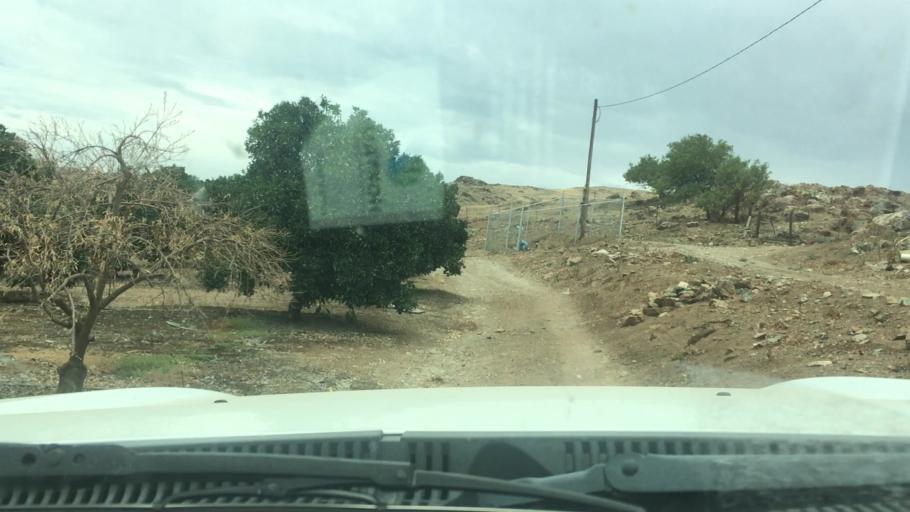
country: US
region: California
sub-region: Tulare County
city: Porterville
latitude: 36.0999
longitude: -119.0124
